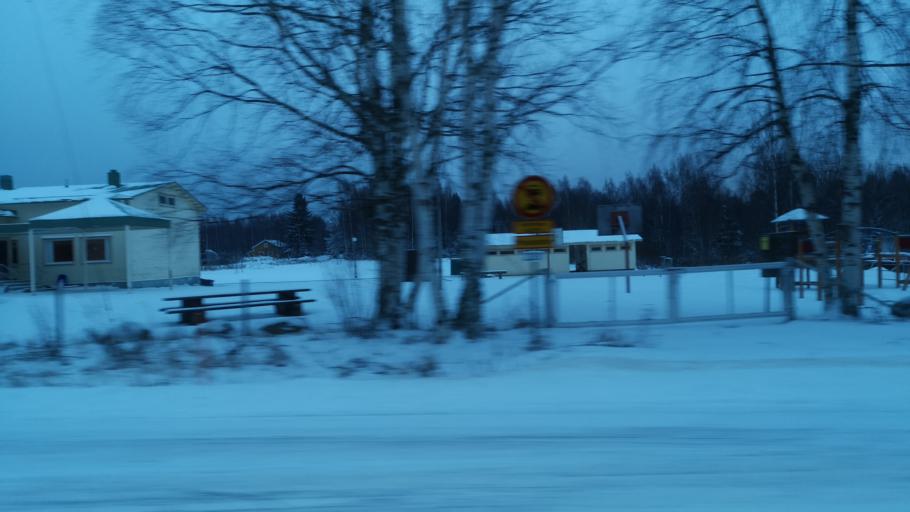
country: FI
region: Southern Savonia
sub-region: Savonlinna
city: Enonkoski
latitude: 62.0685
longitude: 28.7378
